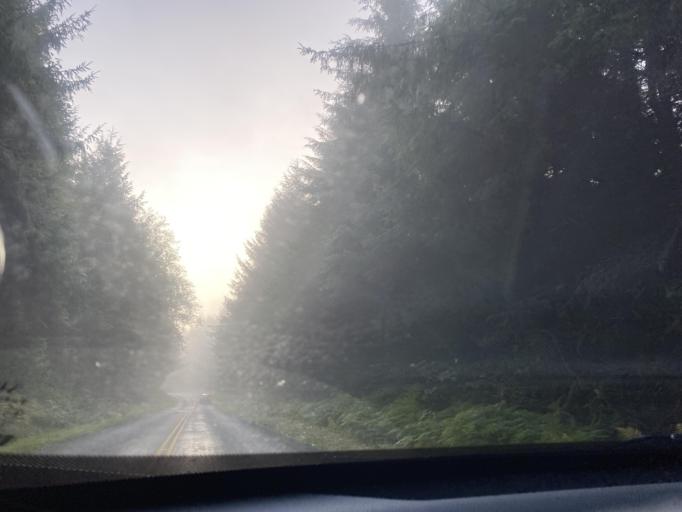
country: US
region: Washington
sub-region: Clallam County
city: Forks
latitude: 47.8096
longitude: -124.0876
